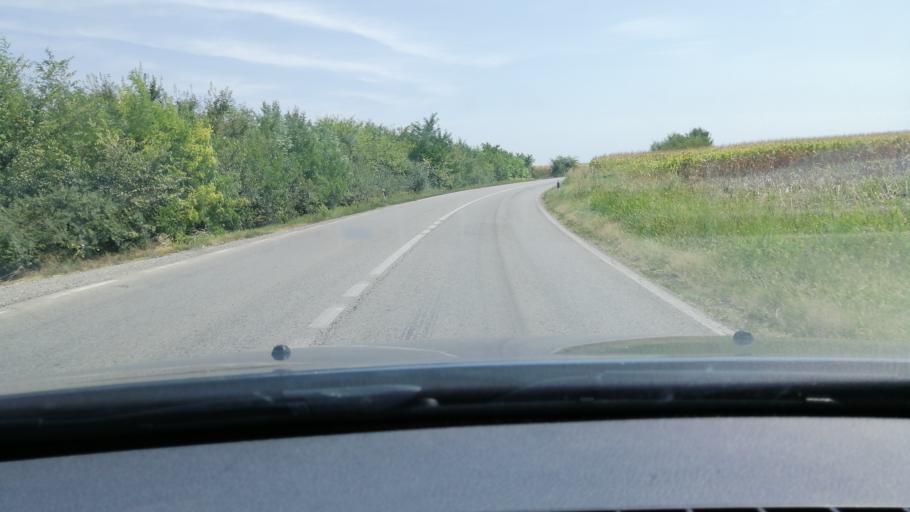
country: RS
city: Sutjeska
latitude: 45.3818
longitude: 20.7258
